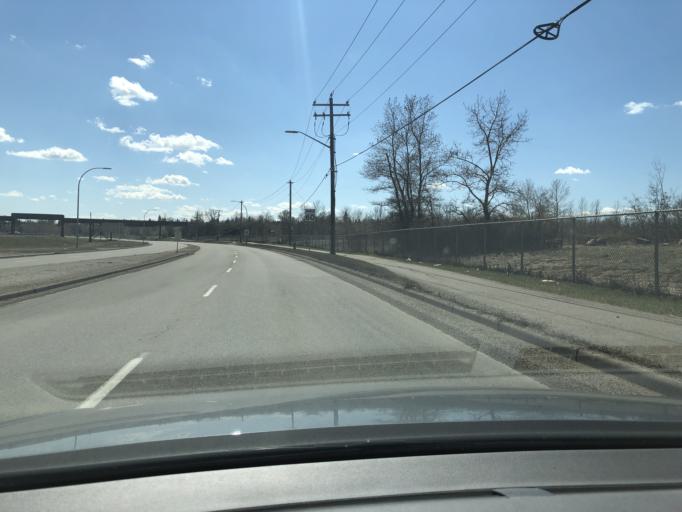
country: CA
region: Alberta
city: Calgary
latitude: 51.0053
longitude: -114.0124
